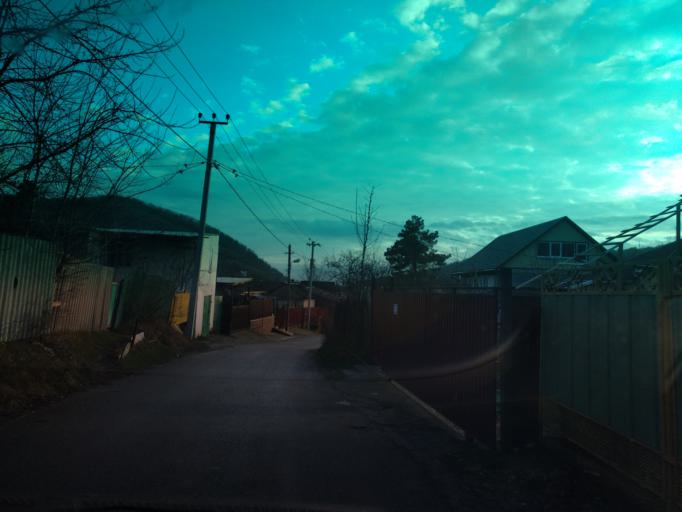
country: RU
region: Krasnodarskiy
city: Novomikhaylovskiy
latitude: 44.2743
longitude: 38.8344
